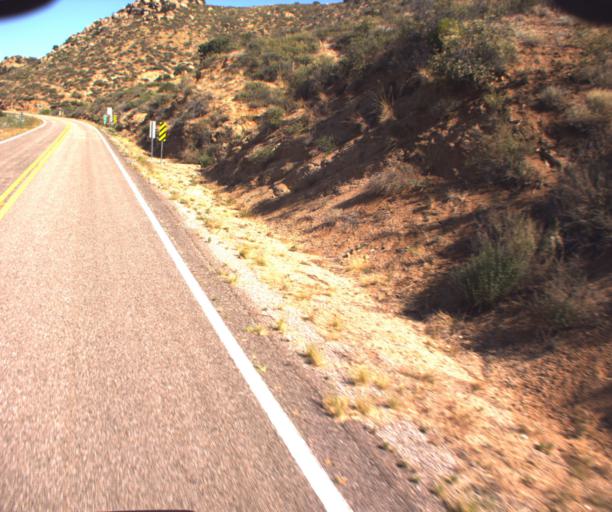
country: US
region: Arizona
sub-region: Graham County
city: Swift Trail Junction
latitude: 32.5756
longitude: -109.8405
